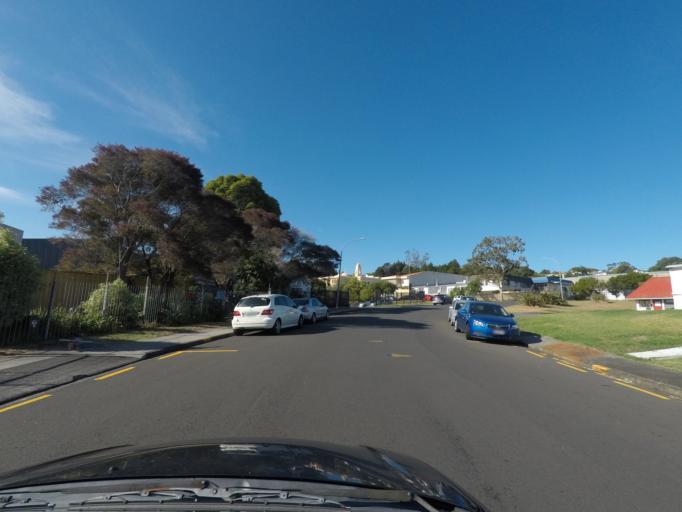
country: NZ
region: Auckland
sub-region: Auckland
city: Rosebank
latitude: -36.9044
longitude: 174.6984
